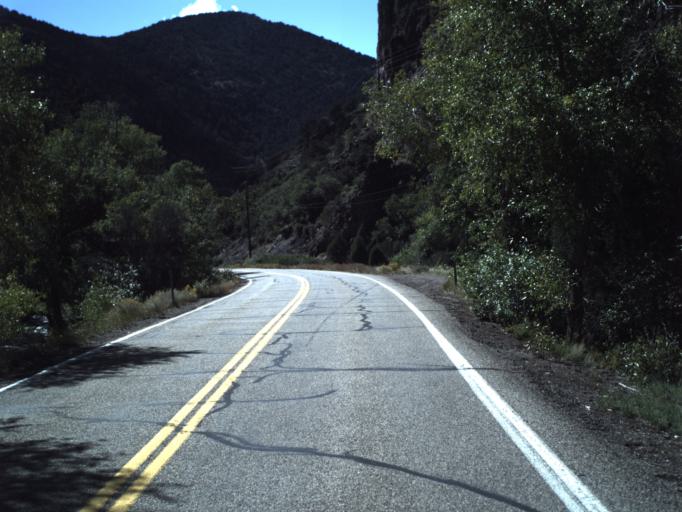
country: US
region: Utah
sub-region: Beaver County
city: Beaver
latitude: 38.2541
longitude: -112.5296
